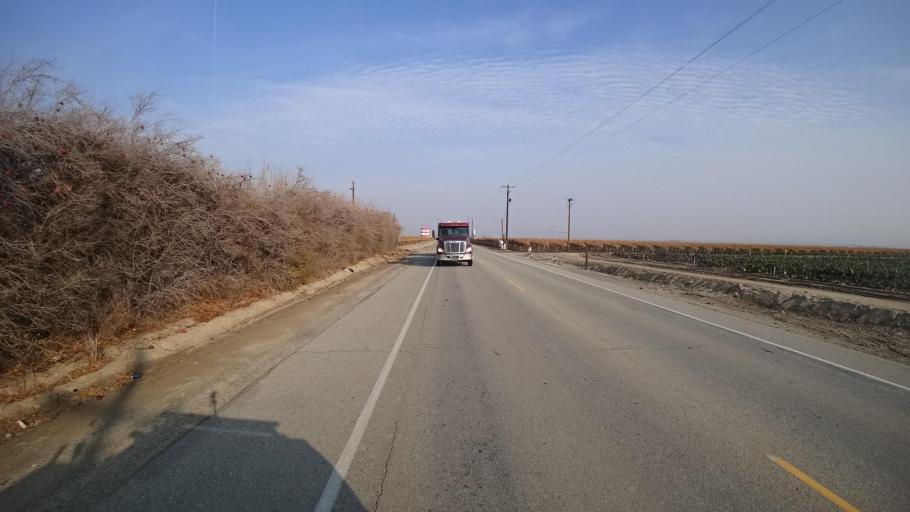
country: US
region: California
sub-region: Kern County
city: Arvin
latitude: 35.0595
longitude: -118.9175
